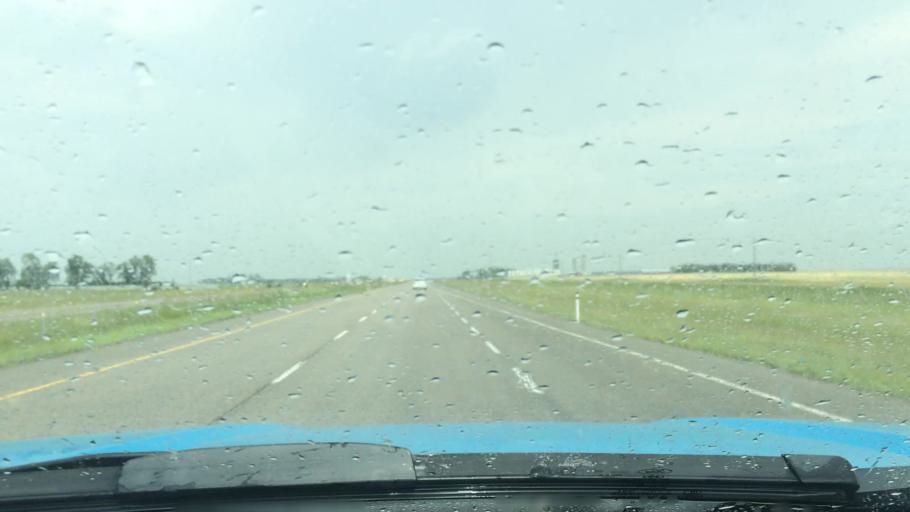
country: CA
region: Alberta
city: Olds
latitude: 51.7094
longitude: -114.0253
